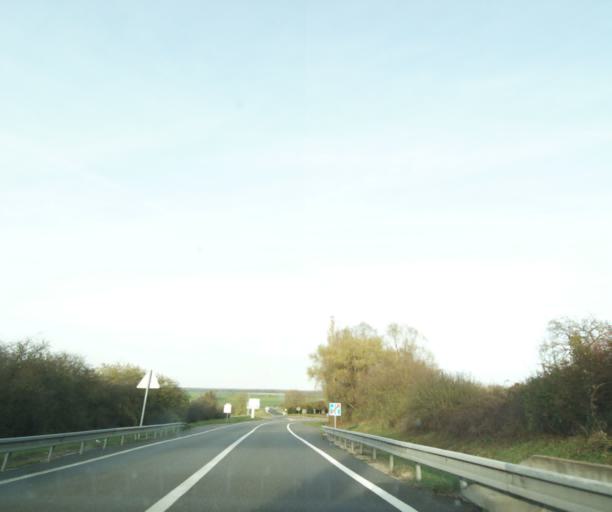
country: FR
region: Lorraine
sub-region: Departement de la Meuse
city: Etain
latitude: 49.1313
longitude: 5.6234
